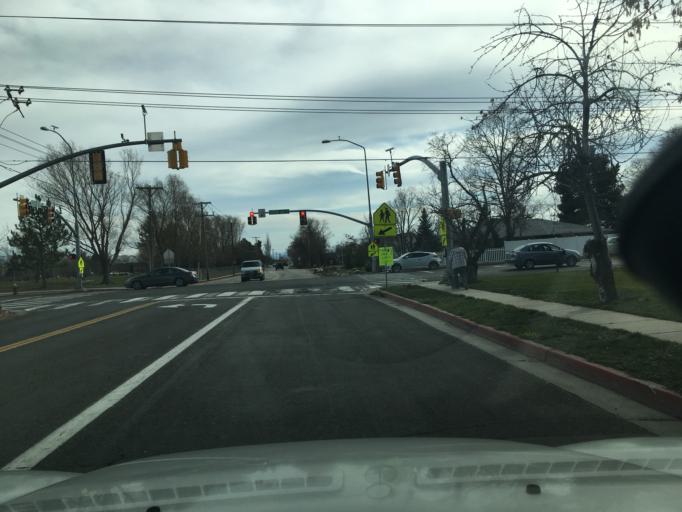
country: US
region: Utah
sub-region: Davis County
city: Layton
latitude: 41.0750
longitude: -112.0070
